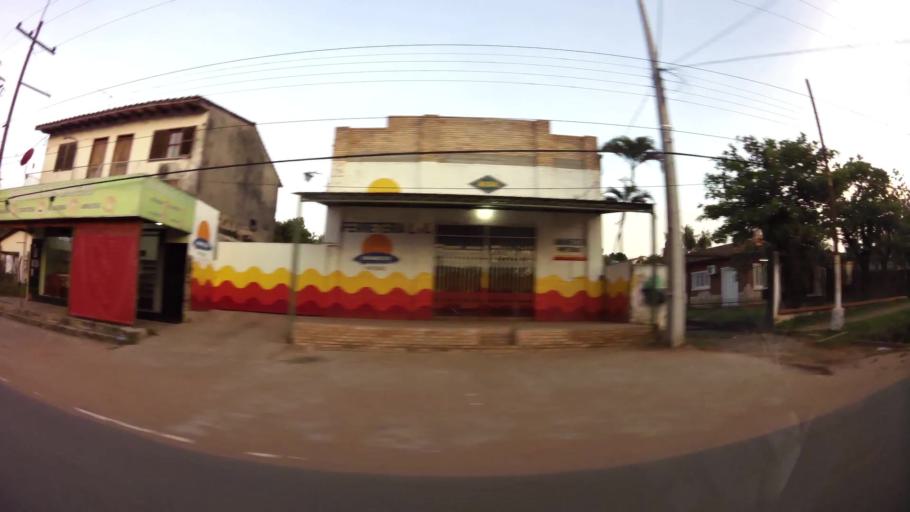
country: PY
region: Central
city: Nemby
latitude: -25.3844
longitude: -57.4960
